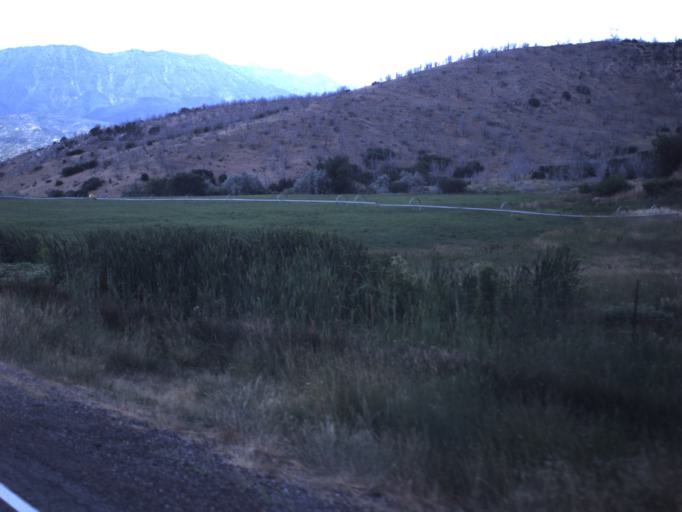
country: US
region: Utah
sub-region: Sanpete County
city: Fountain Green
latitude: 39.7069
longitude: -111.7124
